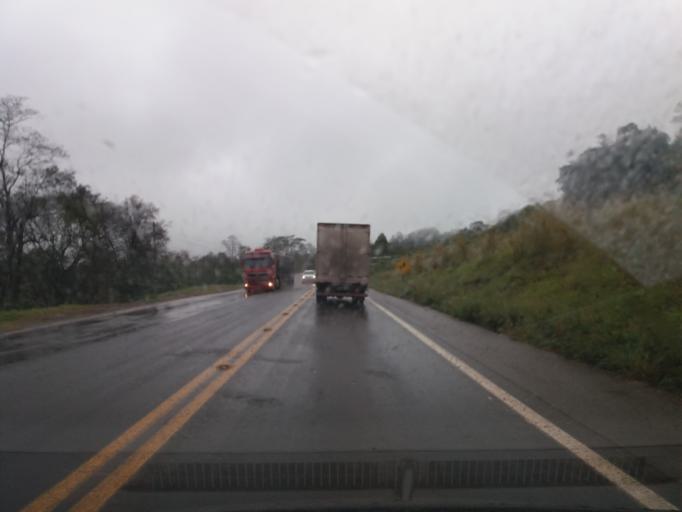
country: BR
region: Parana
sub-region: Realeza
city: Realeza
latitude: -25.4786
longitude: -53.5911
